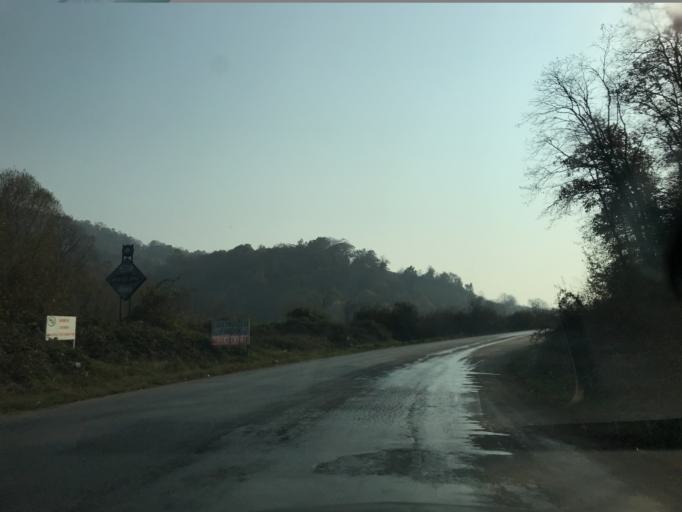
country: TR
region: Duzce
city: Cumayeri
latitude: 40.8942
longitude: 30.9567
